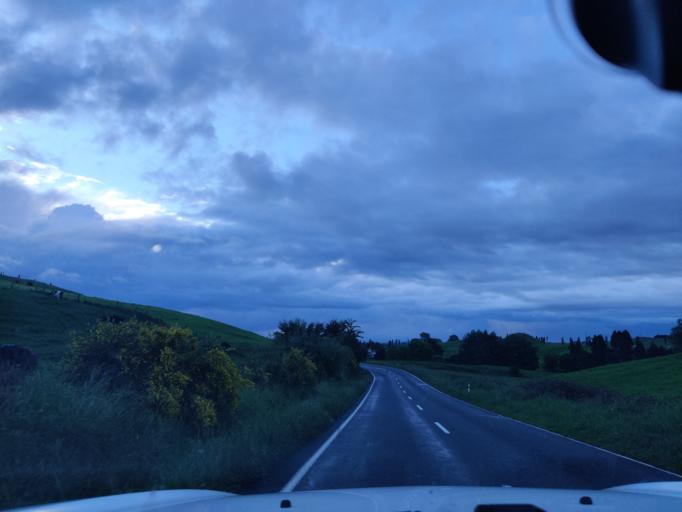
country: NZ
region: Waikato
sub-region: South Waikato District
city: Tokoroa
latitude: -38.2115
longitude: 175.8251
